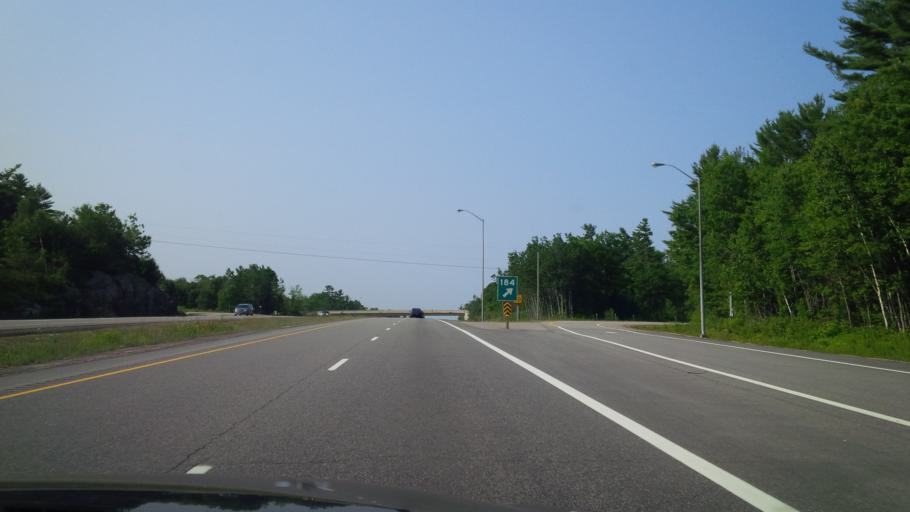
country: CA
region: Ontario
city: Bracebridge
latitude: 45.0154
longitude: -79.2958
